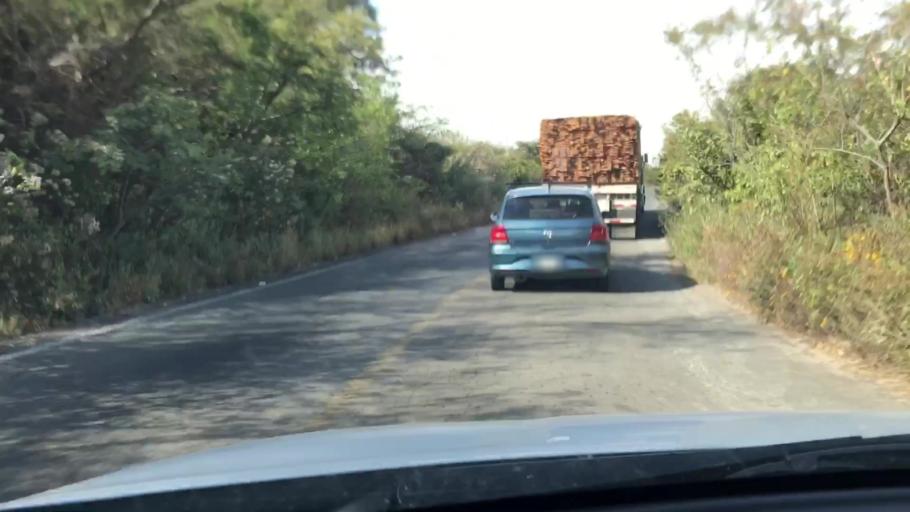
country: MX
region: Jalisco
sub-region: Zacoalco de Torres
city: Barranca de Otates (Barranca de Otatan)
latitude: 20.2318
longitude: -103.6839
